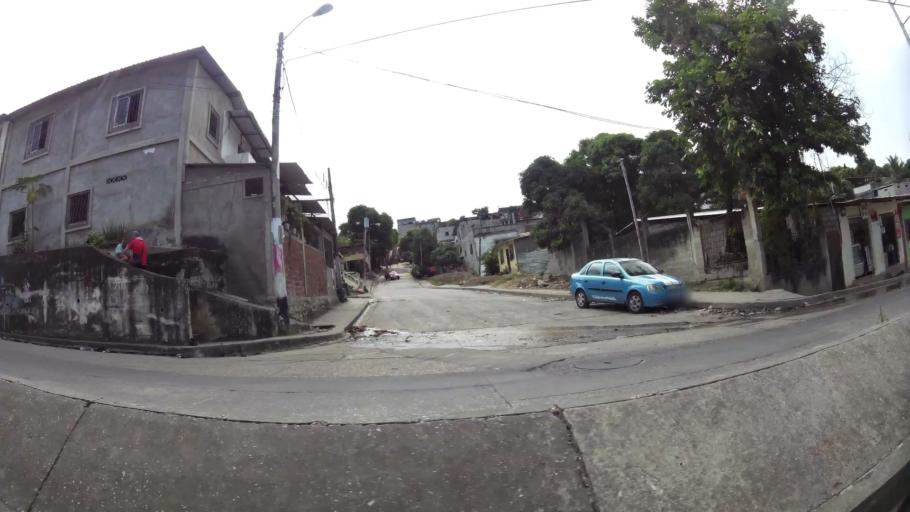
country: EC
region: Guayas
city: Santa Lucia
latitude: -2.1341
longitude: -79.9456
